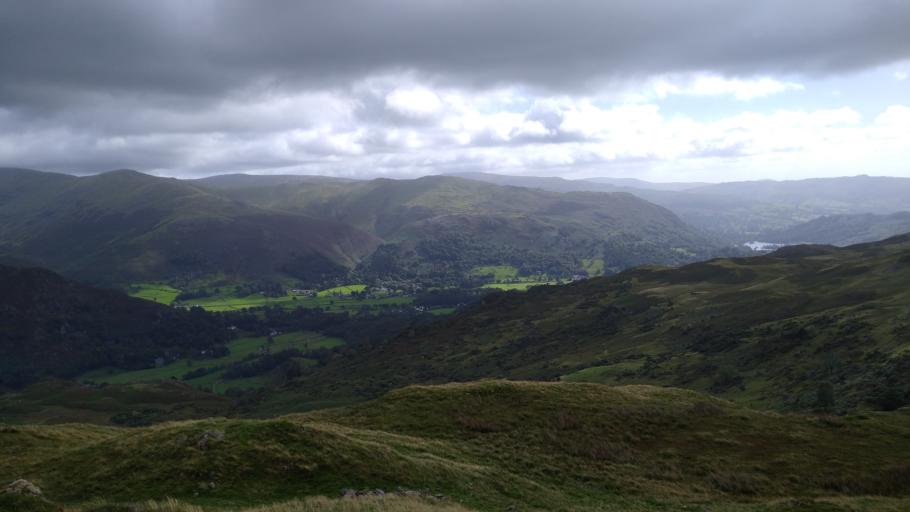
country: GB
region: England
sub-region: Cumbria
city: Ambleside
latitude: 54.4585
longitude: -3.0645
